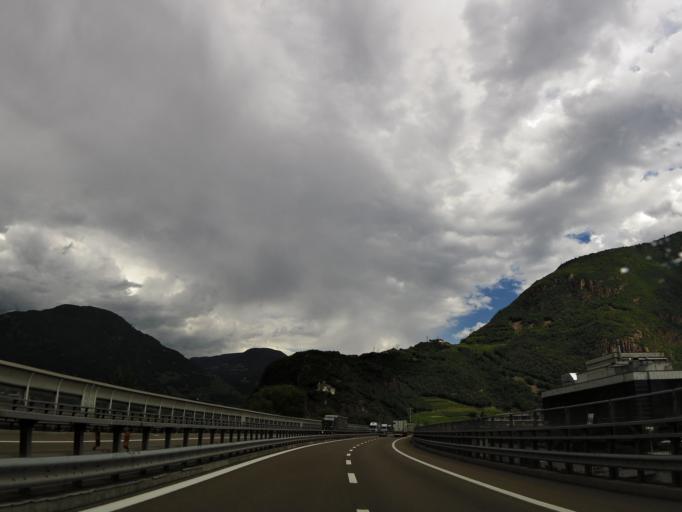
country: IT
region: Trentino-Alto Adige
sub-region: Bolzano
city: Bolzano
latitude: 46.4875
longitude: 11.3390
